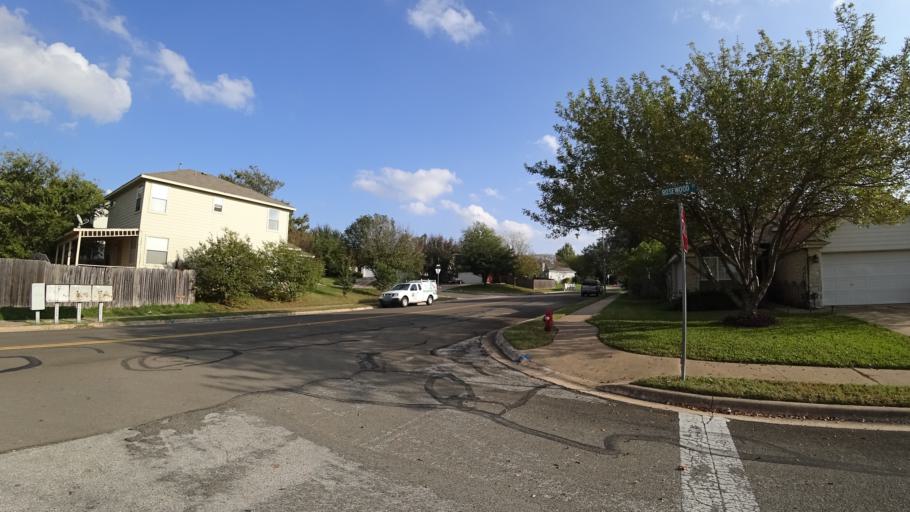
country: US
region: Texas
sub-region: Williamson County
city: Round Rock
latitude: 30.4902
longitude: -97.6573
